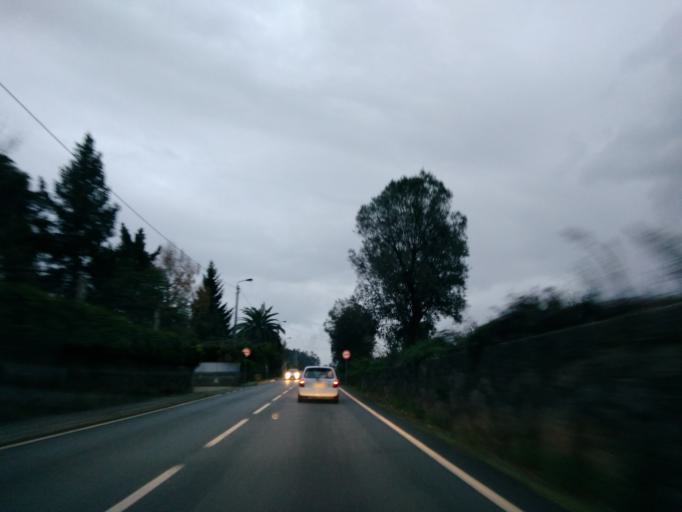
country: PT
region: Braga
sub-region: Braga
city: Oliveira
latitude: 41.4792
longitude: -8.4818
